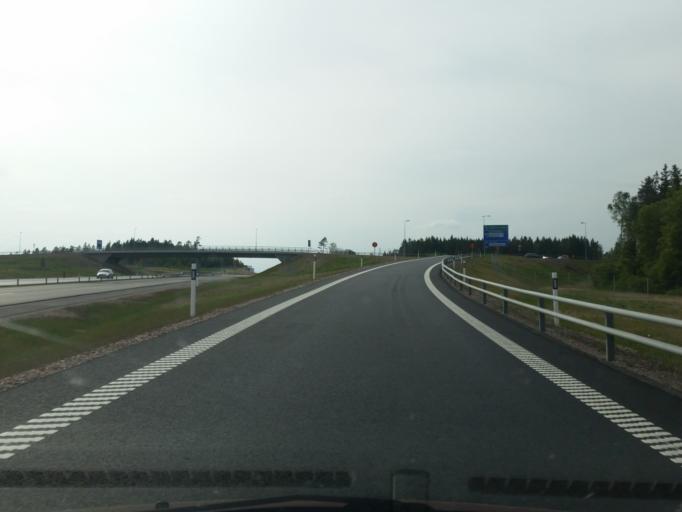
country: SE
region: Vaestra Goetaland
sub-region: Ulricehamns Kommun
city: Ulricehamn
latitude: 57.8038
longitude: 13.4751
